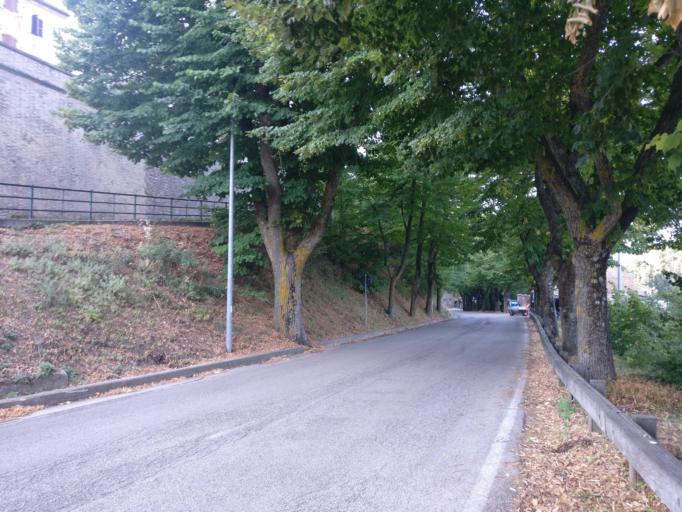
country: IT
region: The Marches
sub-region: Provincia di Ascoli Piceno
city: Montalto delle Marche
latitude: 42.9874
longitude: 13.6059
